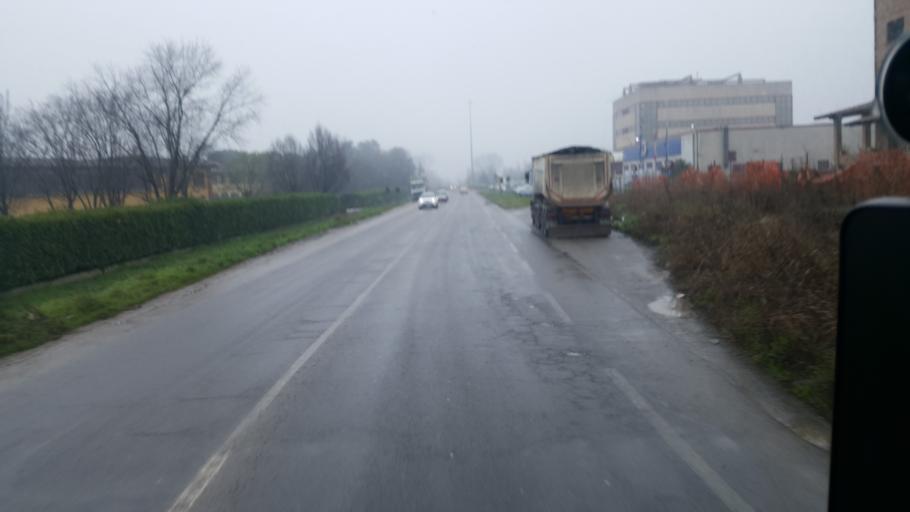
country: IT
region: Lombardy
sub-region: Provincia di Pavia
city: Landriano
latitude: 45.3092
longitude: 9.2711
